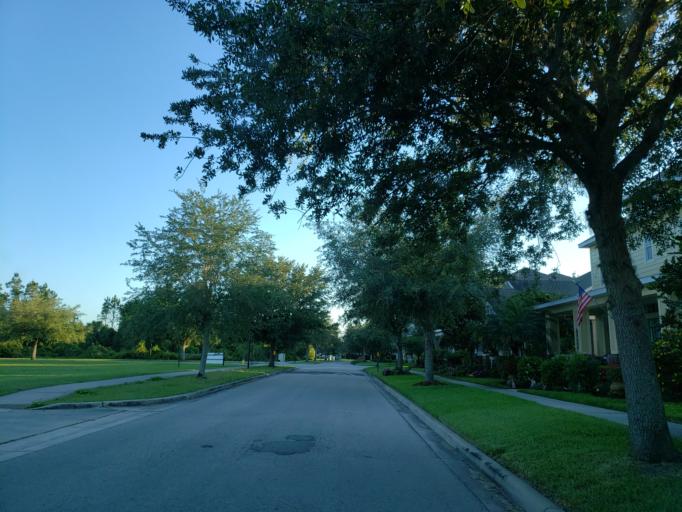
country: US
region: Florida
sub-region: Hillsborough County
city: Fish Hawk
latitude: 27.8403
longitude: -82.2134
